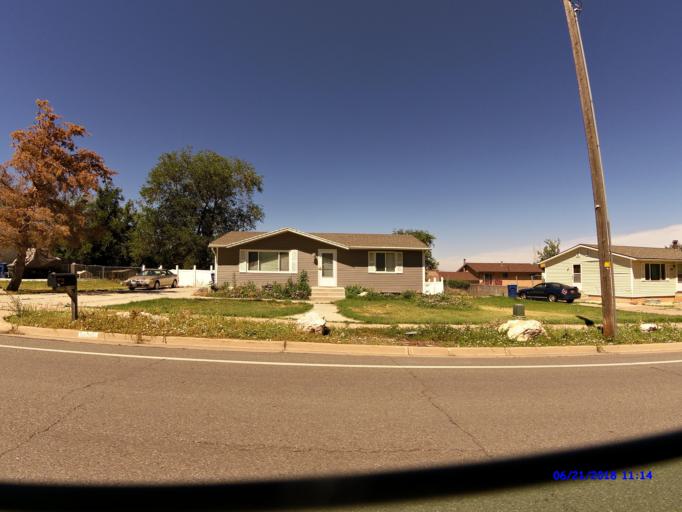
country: US
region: Utah
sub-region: Weber County
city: North Ogden
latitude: 41.2786
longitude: -111.9589
